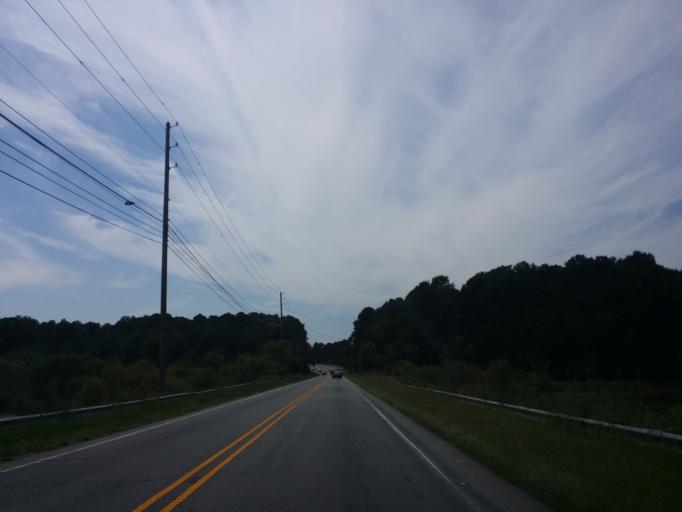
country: US
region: North Carolina
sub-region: Wake County
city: Morrisville
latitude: 35.8423
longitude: -78.8053
